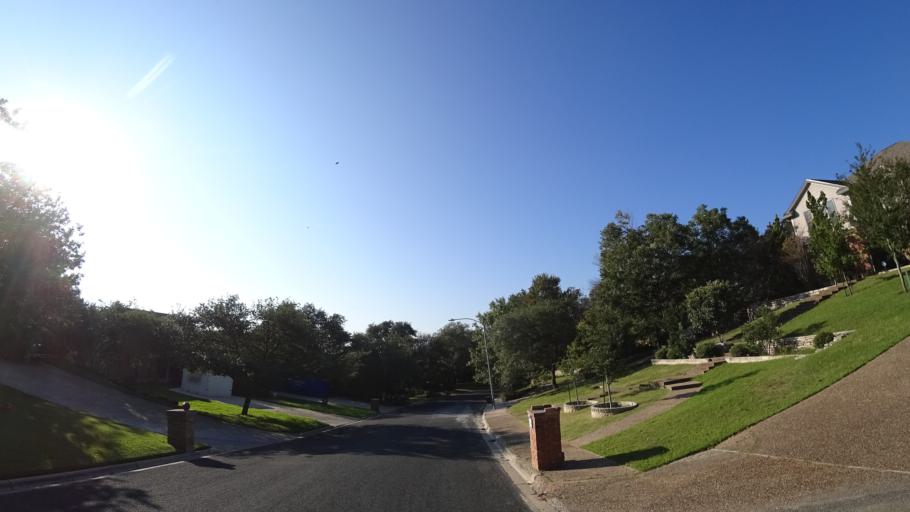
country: US
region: Texas
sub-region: Travis County
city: Rollingwood
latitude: 30.2627
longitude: -97.7985
